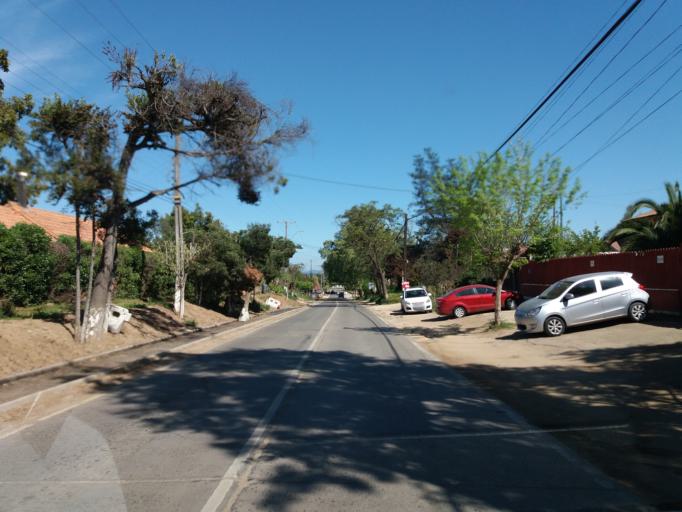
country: CL
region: Valparaiso
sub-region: Provincia de Marga Marga
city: Limache
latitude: -33.0007
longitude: -71.2032
